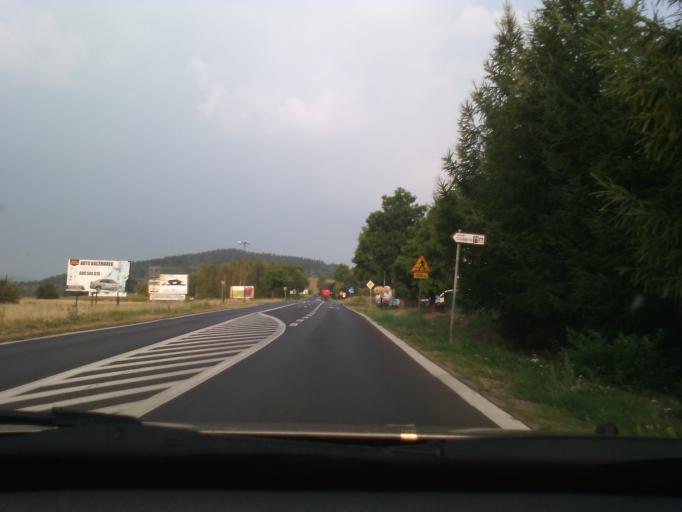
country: PL
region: Lower Silesian Voivodeship
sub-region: Jelenia Gora
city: Cieplice Slaskie Zdroj
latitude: 50.8923
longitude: 15.6841
